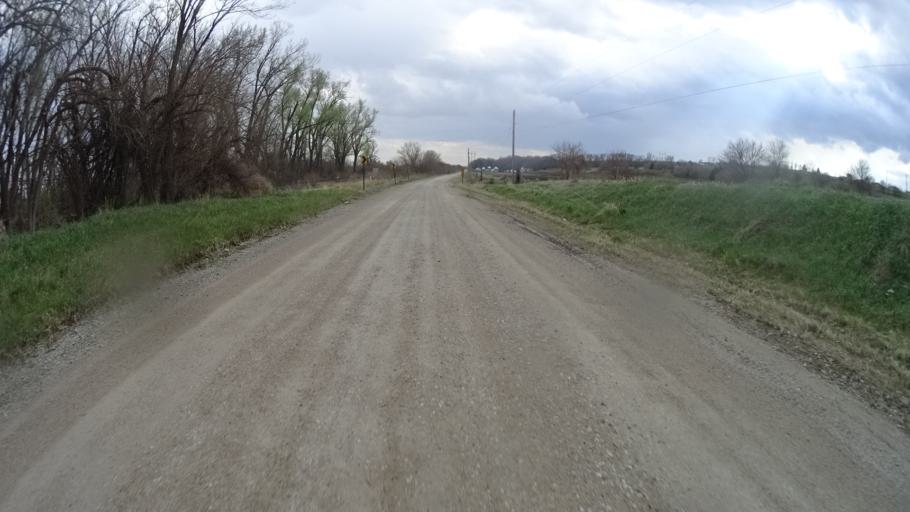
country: US
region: Nebraska
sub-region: Sarpy County
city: Offutt Air Force Base
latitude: 41.0934
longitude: -95.9138
